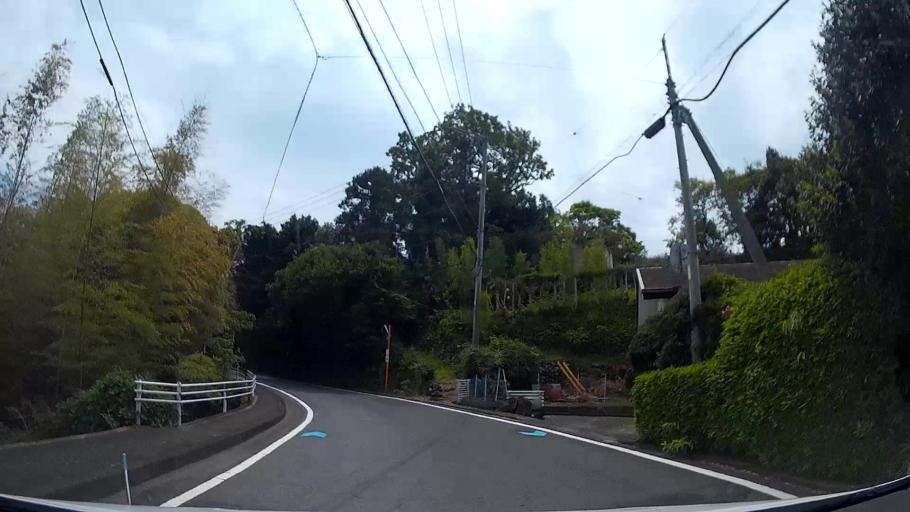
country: JP
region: Shizuoka
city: Ito
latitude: 34.8950
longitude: 139.1310
